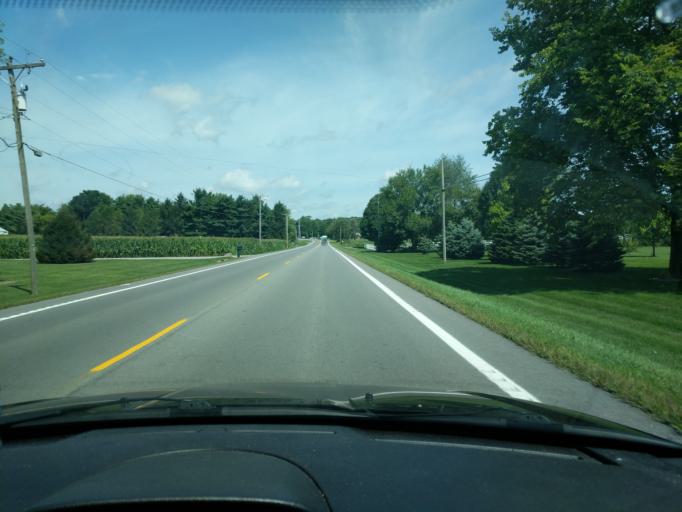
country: US
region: Ohio
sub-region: Logan County
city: West Liberty
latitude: 40.2977
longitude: -83.7596
